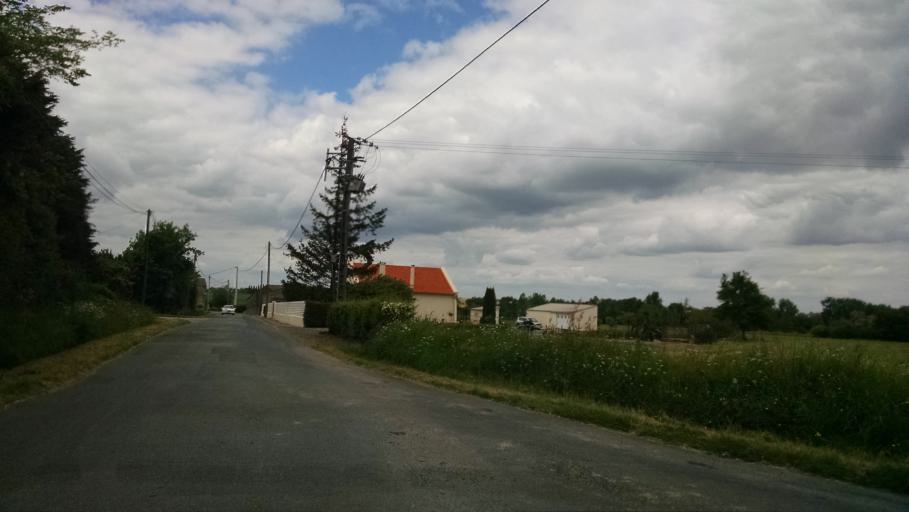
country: FR
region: Pays de la Loire
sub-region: Departement de la Loire-Atlantique
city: Remouille
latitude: 47.0450
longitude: -1.3827
